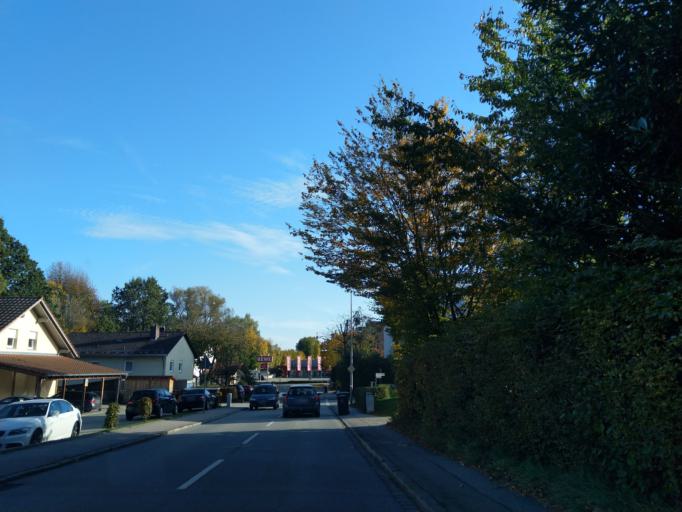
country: DE
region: Bavaria
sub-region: Lower Bavaria
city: Deggendorf
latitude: 48.8470
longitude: 12.9499
